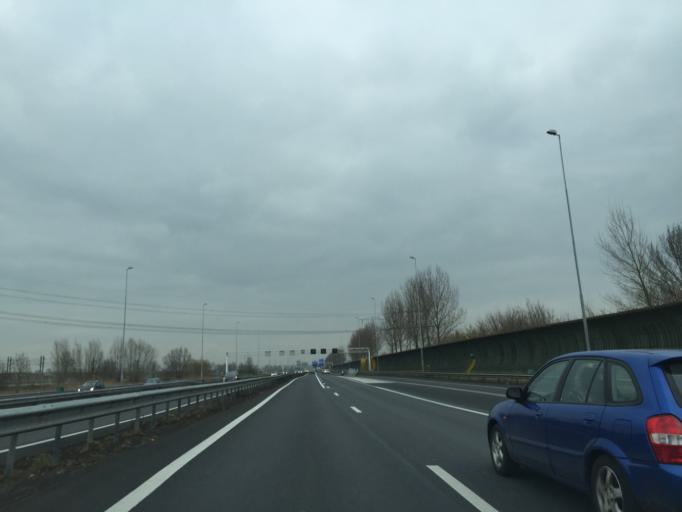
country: NL
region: South Holland
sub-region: Gemeente Papendrecht
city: Papendrecht
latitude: 51.8381
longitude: 4.7172
